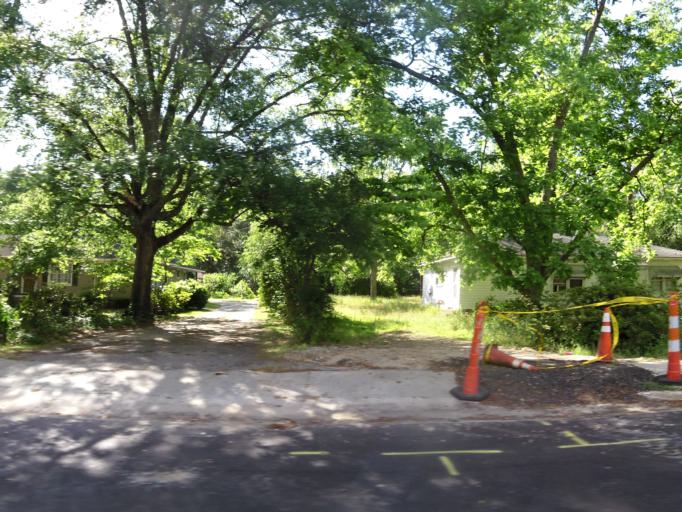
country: US
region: South Carolina
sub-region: Allendale County
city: Fairfax
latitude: 32.9712
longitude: -81.2327
